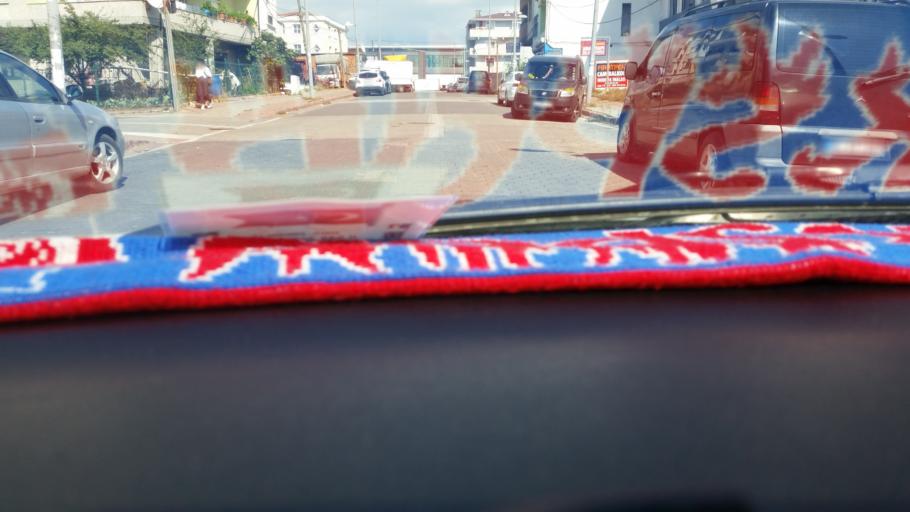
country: TR
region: Istanbul
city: Esenyurt
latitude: 41.0775
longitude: 28.6330
